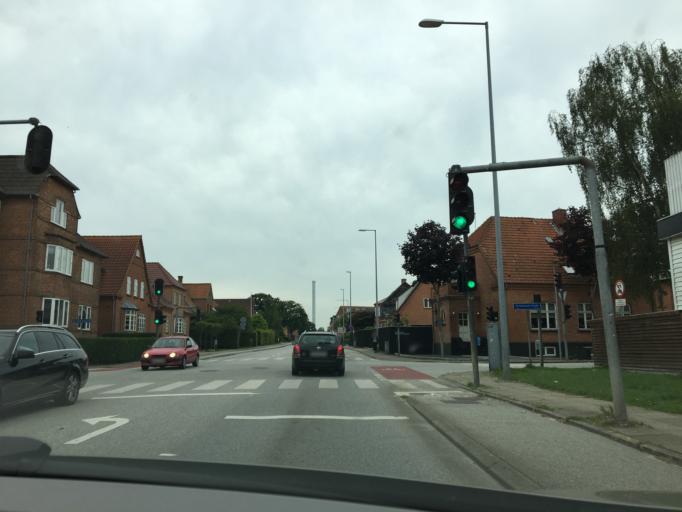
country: DK
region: Central Jutland
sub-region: Herning Kommune
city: Herning
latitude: 56.1370
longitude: 8.9872
